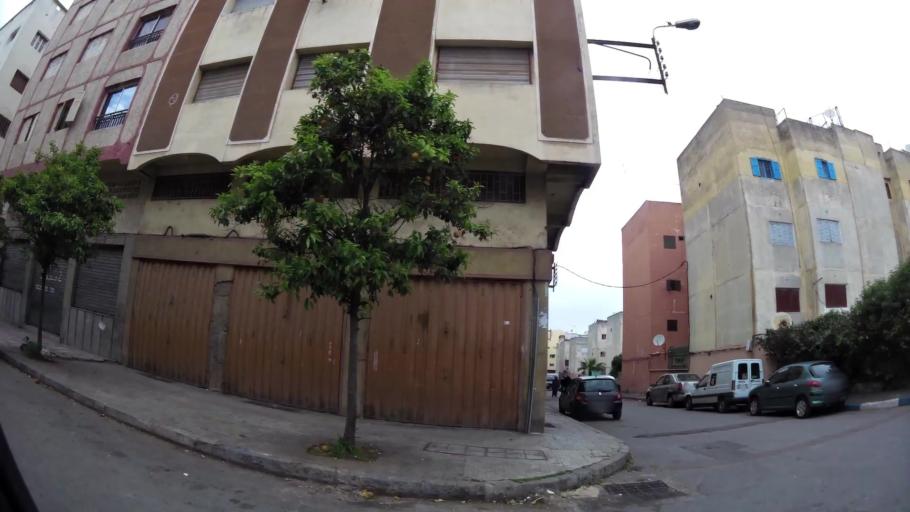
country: MA
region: Grand Casablanca
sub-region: Casablanca
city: Casablanca
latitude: 33.5747
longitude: -7.5677
